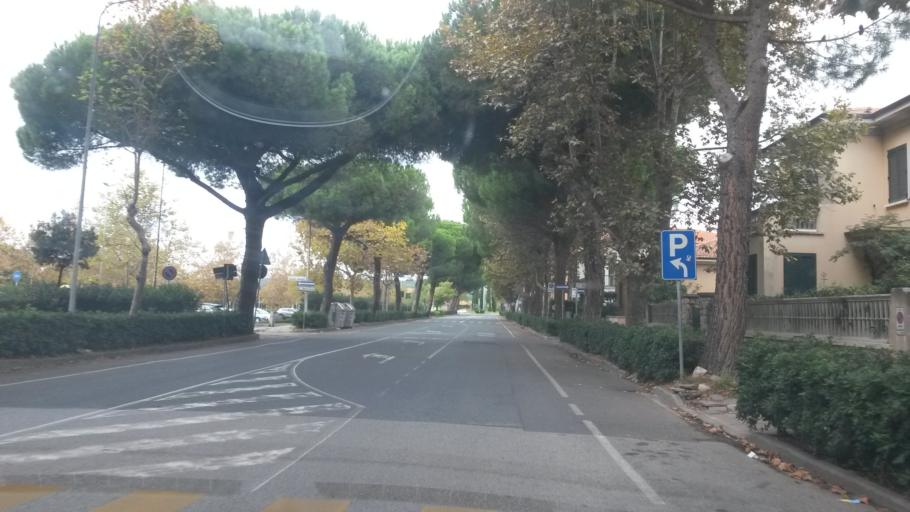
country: IT
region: Tuscany
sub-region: Provincia di Livorno
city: Rosignano Solvay-Castiglioncello
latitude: 43.3953
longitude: 10.4368
